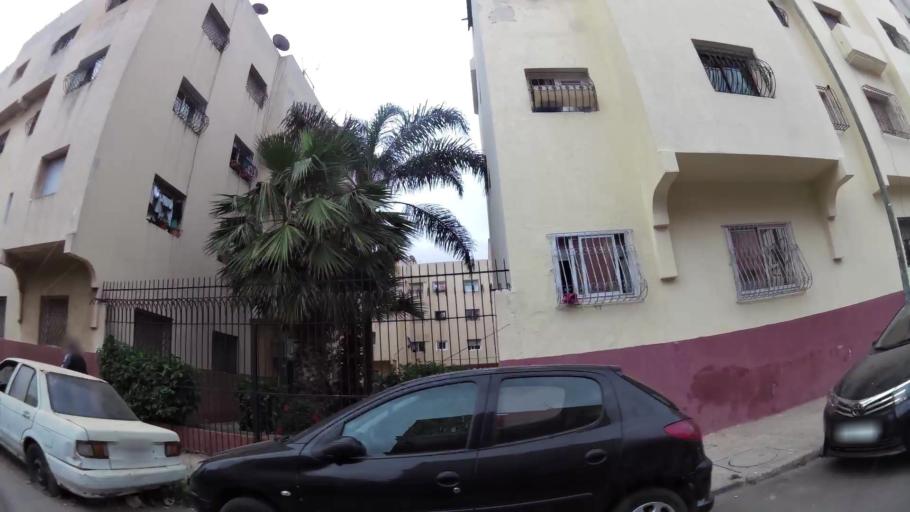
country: MA
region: Rabat-Sale-Zemmour-Zaer
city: Sale
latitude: 34.0394
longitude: -6.8025
